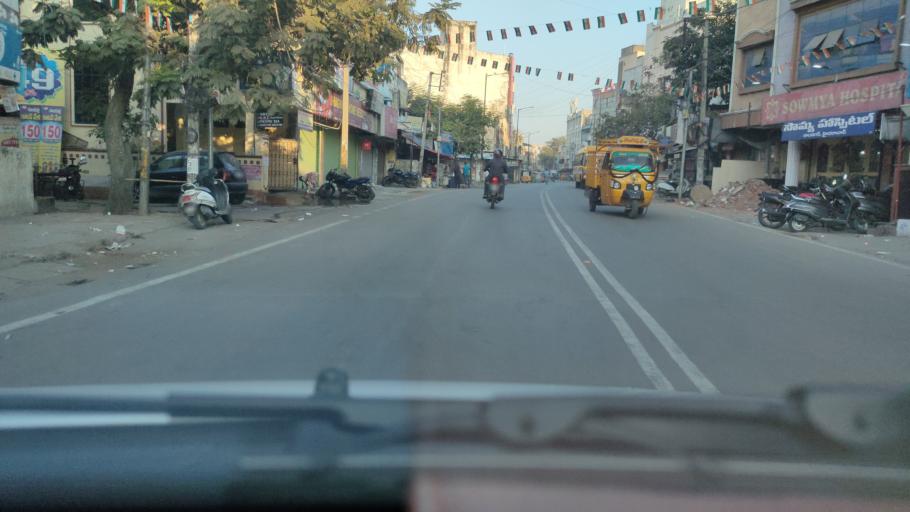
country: IN
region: Telangana
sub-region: Hyderabad
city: Malkajgiri
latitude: 17.4095
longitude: 78.5085
